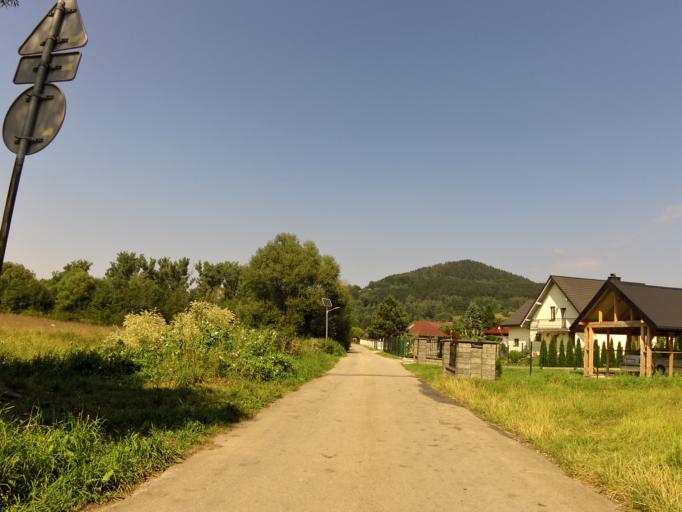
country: PL
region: Silesian Voivodeship
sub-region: Powiat zywiecki
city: Wieprz
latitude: 49.6495
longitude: 19.1782
